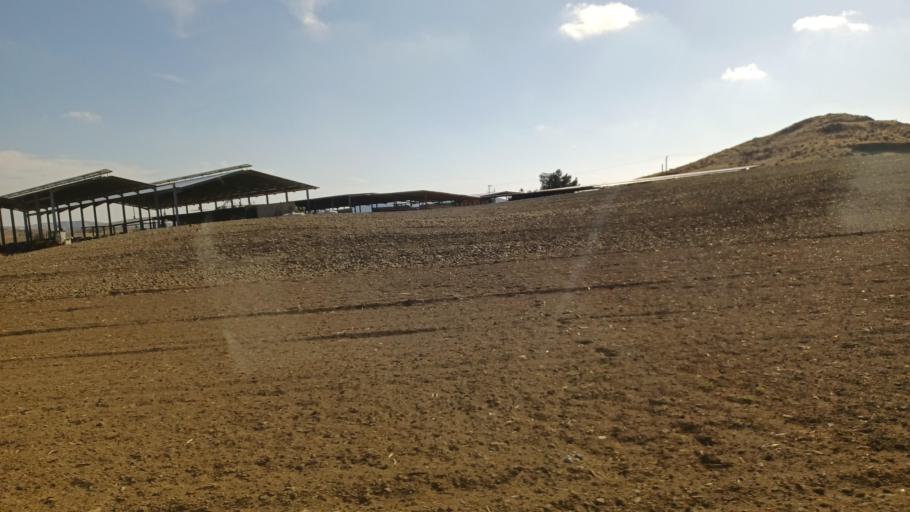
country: CY
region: Larnaka
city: Troulloi
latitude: 35.0194
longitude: 33.5855
